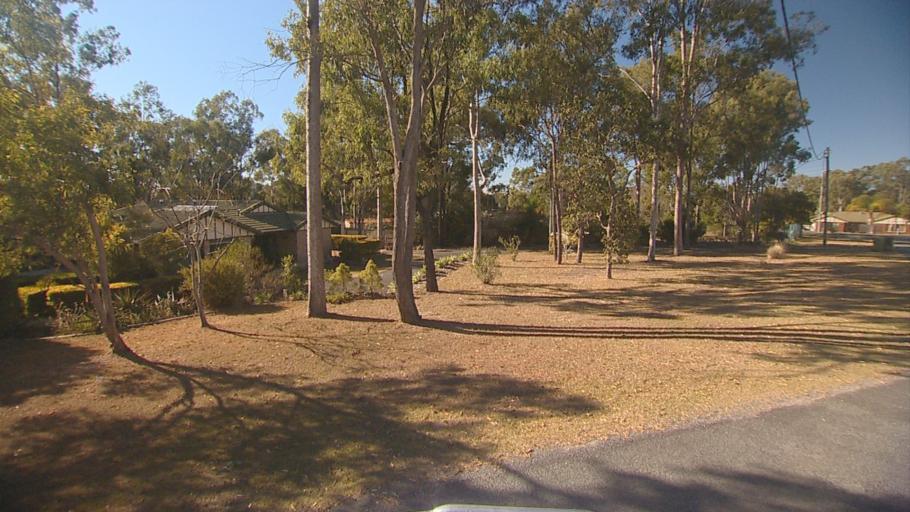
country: AU
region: Queensland
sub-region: Logan
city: North Maclean
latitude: -27.7370
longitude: 152.9639
